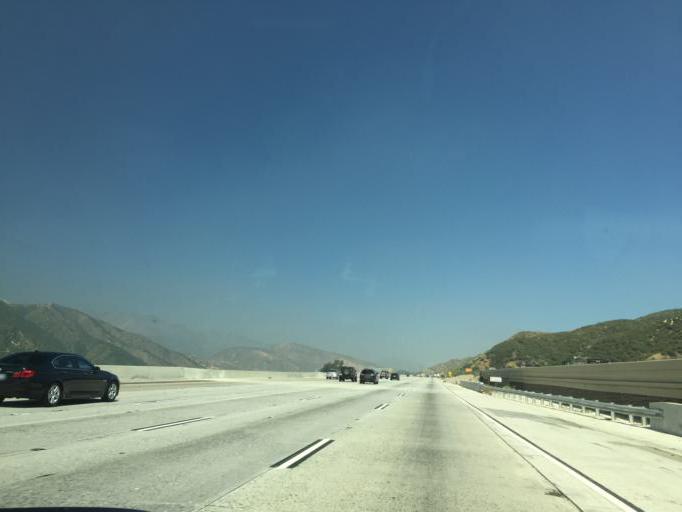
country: US
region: California
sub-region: San Bernardino County
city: Muscoy
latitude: 34.2363
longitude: -117.4242
